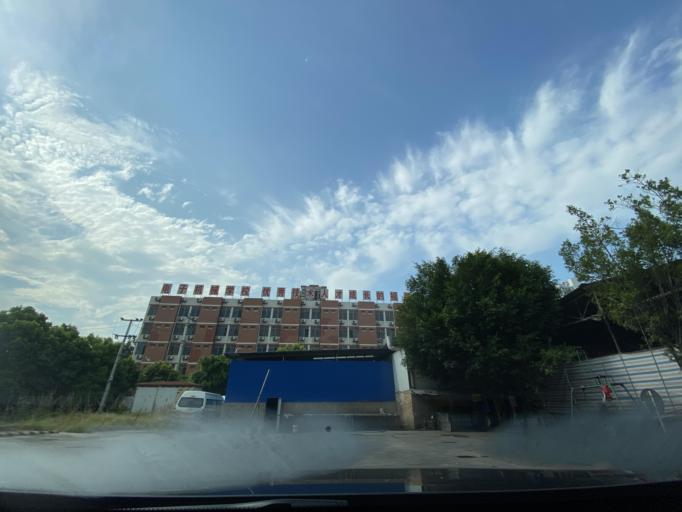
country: CN
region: Sichuan
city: Fuji
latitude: 29.1559
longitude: 105.3658
